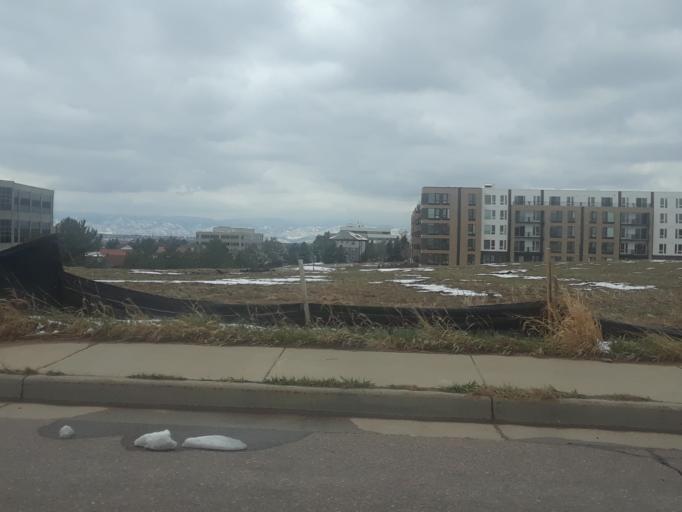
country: US
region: Colorado
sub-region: Arapahoe County
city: Centennial
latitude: 39.5737
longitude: -104.8764
